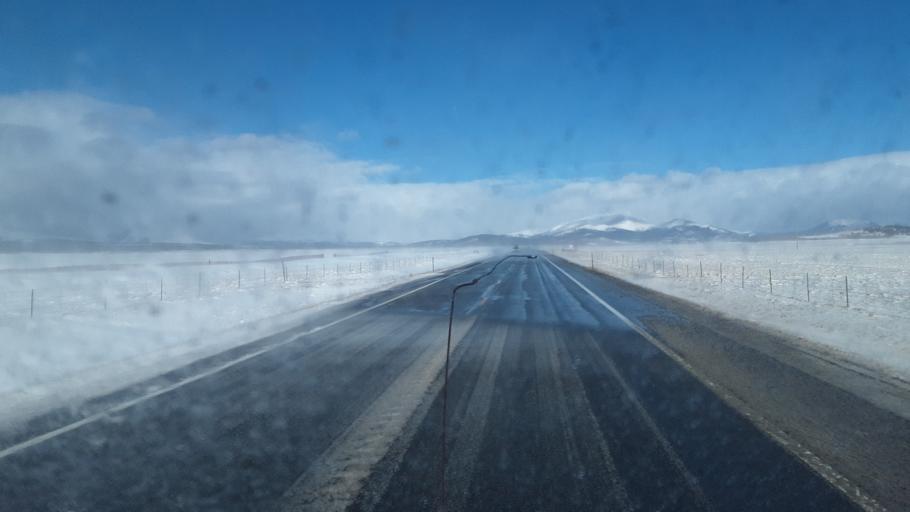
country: US
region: Colorado
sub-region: Park County
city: Fairplay
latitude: 39.1558
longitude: -105.9997
